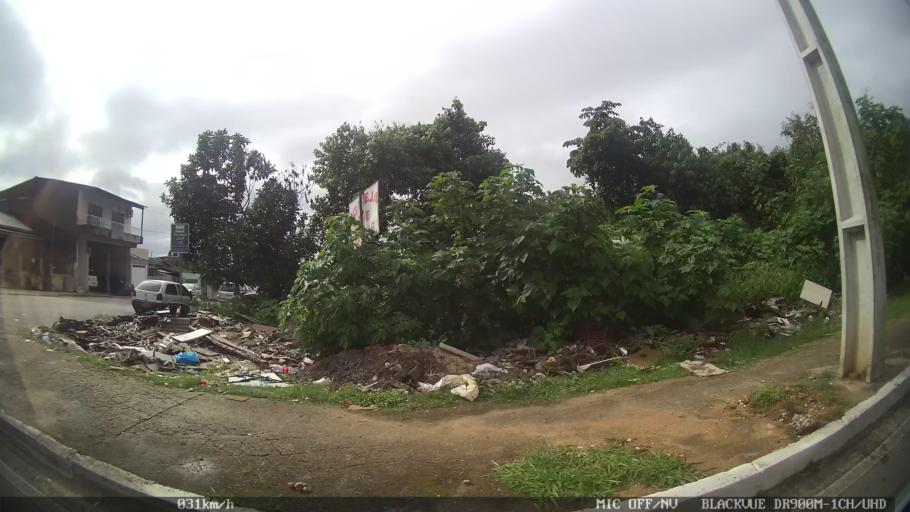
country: BR
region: Santa Catarina
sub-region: Biguacu
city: Biguacu
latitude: -27.5440
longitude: -48.6484
